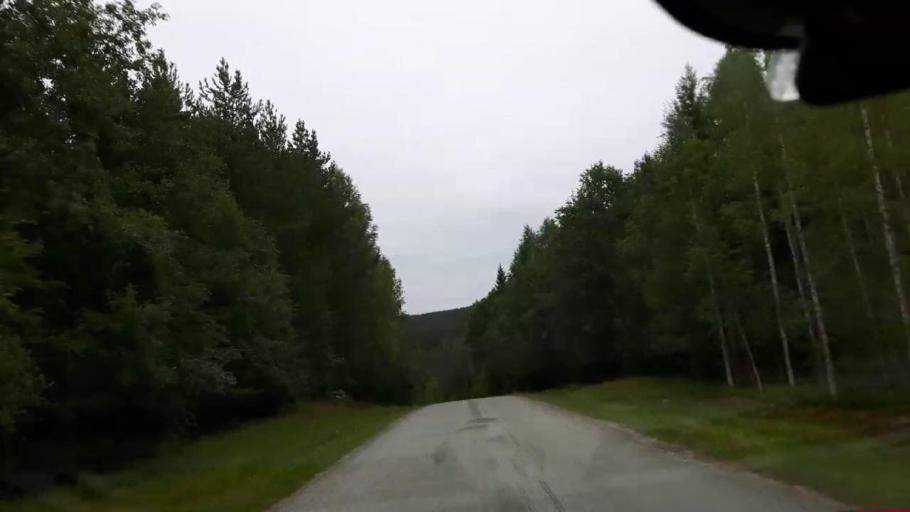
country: SE
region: Vaesternorrland
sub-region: Ange Kommun
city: Fransta
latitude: 62.7774
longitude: 15.9868
